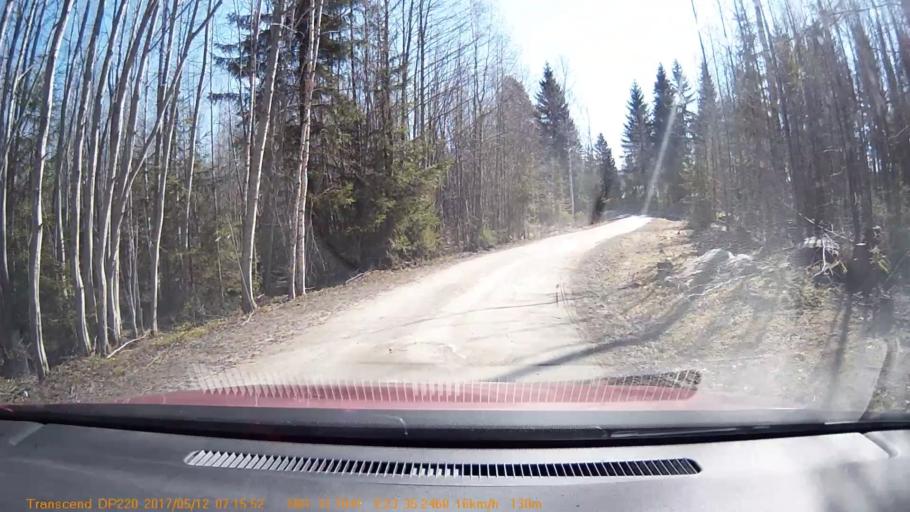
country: FI
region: Pirkanmaa
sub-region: Tampere
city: Yloejaervi
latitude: 61.5284
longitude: 23.5873
